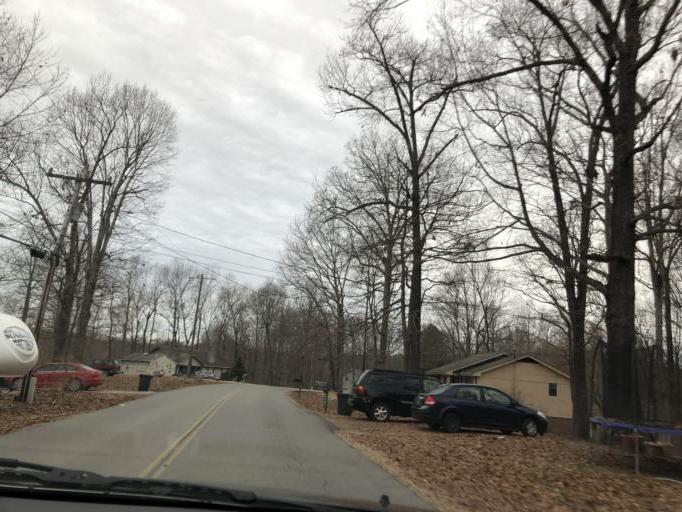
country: US
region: Tennessee
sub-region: Sumner County
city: White House
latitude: 36.4211
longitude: -86.6695
